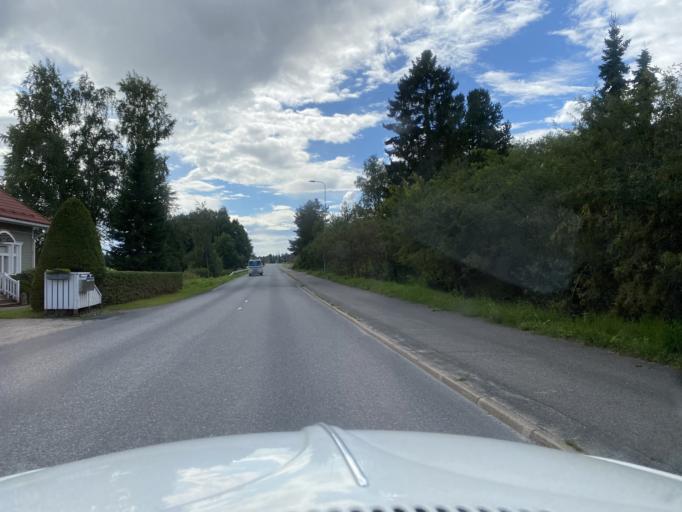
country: FI
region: Satakunta
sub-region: Pori
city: Huittinen
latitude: 61.1721
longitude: 22.6885
